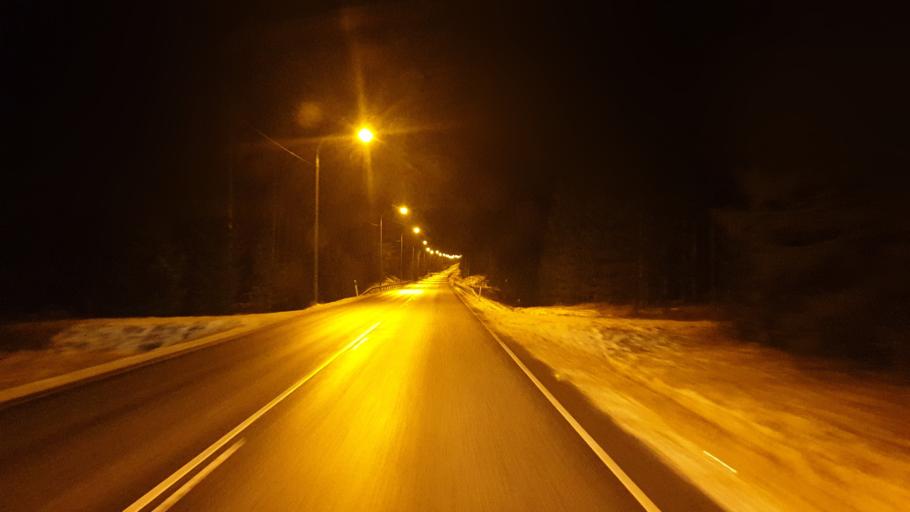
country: FI
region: Northern Savo
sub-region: Sisae-Savo
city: Suonenjoki
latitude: 62.6629
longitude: 27.3533
